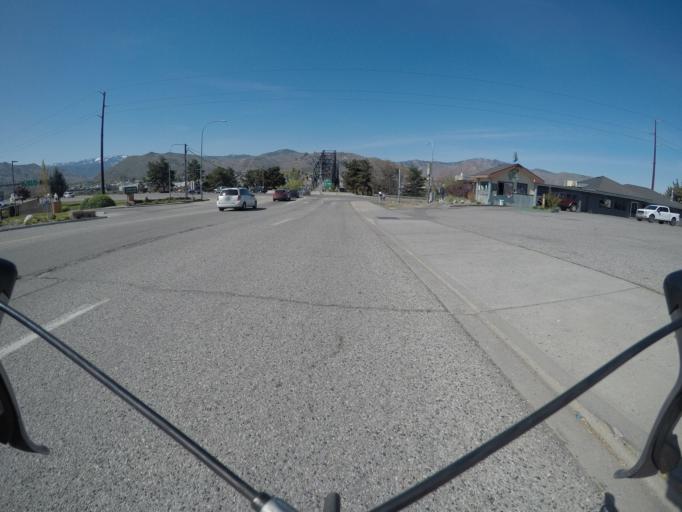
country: US
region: Washington
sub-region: Douglas County
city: East Wenatchee
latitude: 47.4156
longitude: -120.2939
